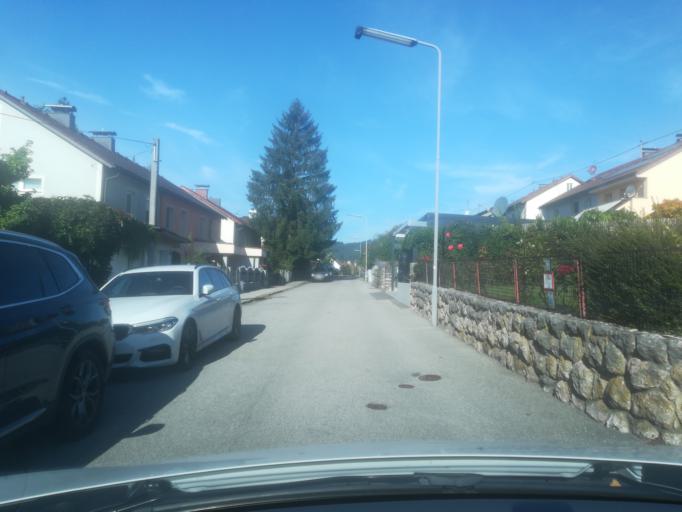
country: AT
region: Upper Austria
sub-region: Politischer Bezirk Linz-Land
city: Leonding
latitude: 48.2802
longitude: 14.2574
